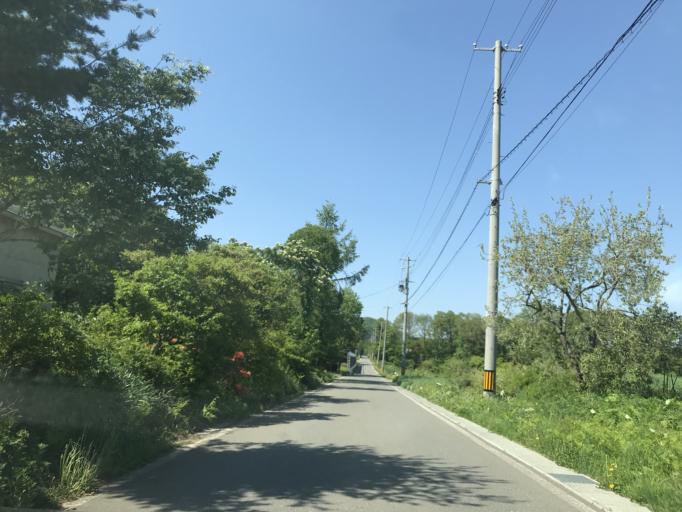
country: JP
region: Iwate
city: Shizukuishi
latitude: 39.5551
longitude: 140.8306
